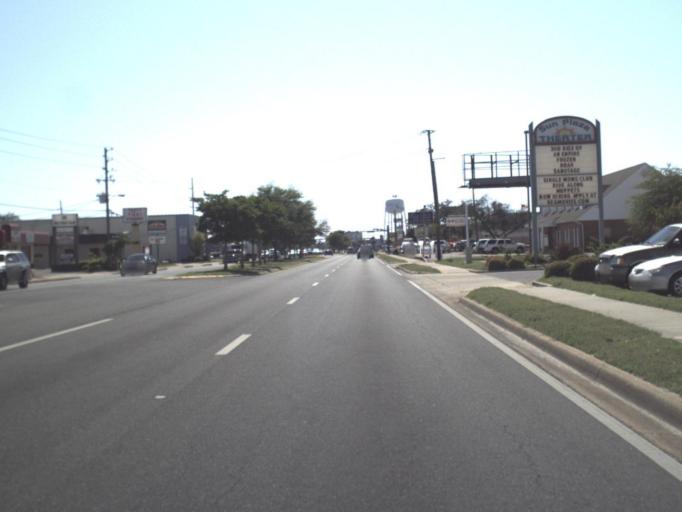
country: US
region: Florida
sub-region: Okaloosa County
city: Mary Esther
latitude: 30.4251
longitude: -86.6446
